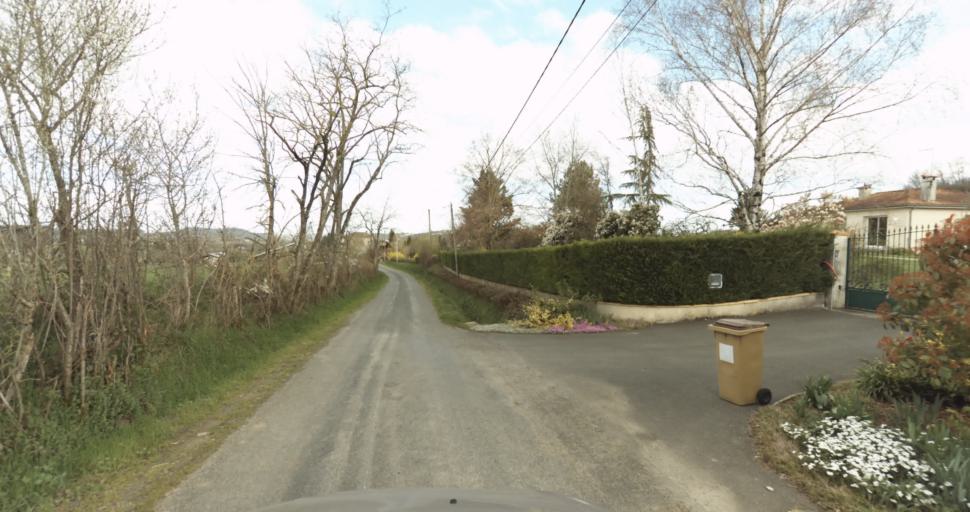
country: FR
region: Midi-Pyrenees
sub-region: Departement du Tarn
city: Puygouzon
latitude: 43.8734
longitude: 2.1845
